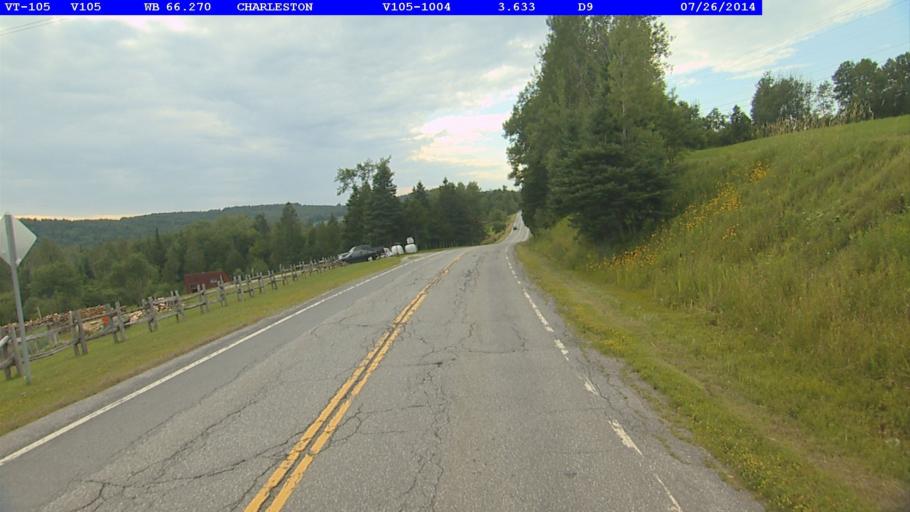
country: US
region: Vermont
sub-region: Orleans County
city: Newport
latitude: 44.8655
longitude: -72.0440
